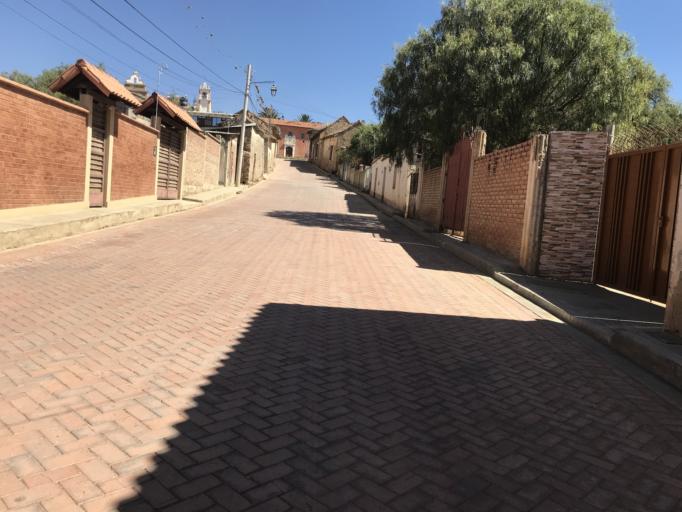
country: BO
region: Cochabamba
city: Tarata
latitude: -17.6148
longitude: -66.0280
